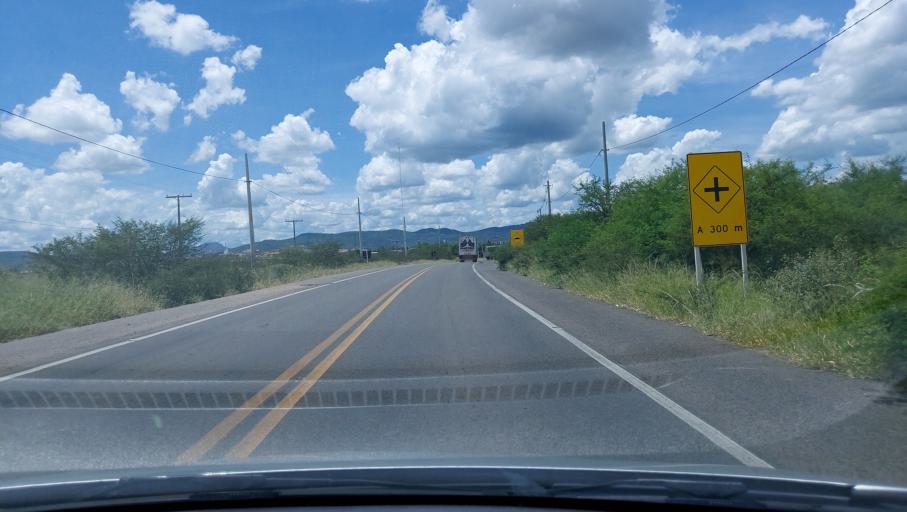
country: BR
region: Bahia
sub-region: Itaberaba
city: Itaberaba
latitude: -12.5209
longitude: -40.2773
